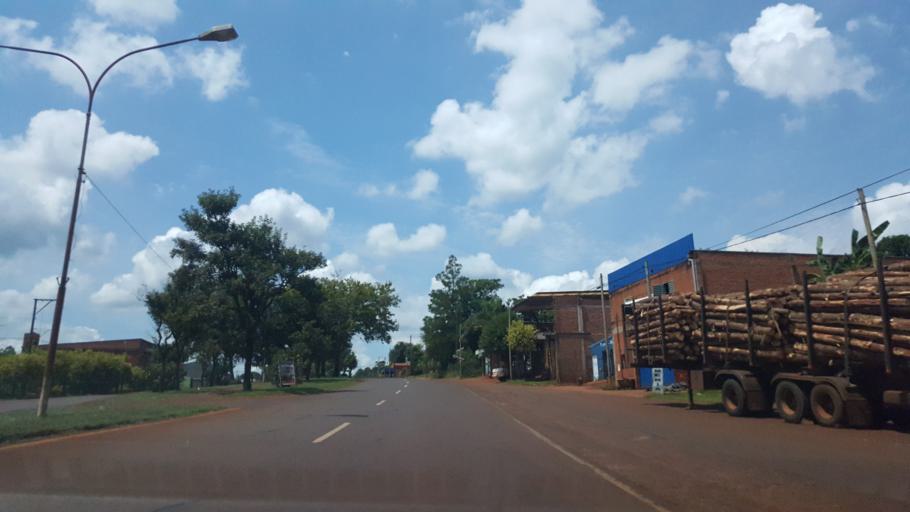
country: AR
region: Misiones
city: Garuhape
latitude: -26.8209
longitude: -54.9612
